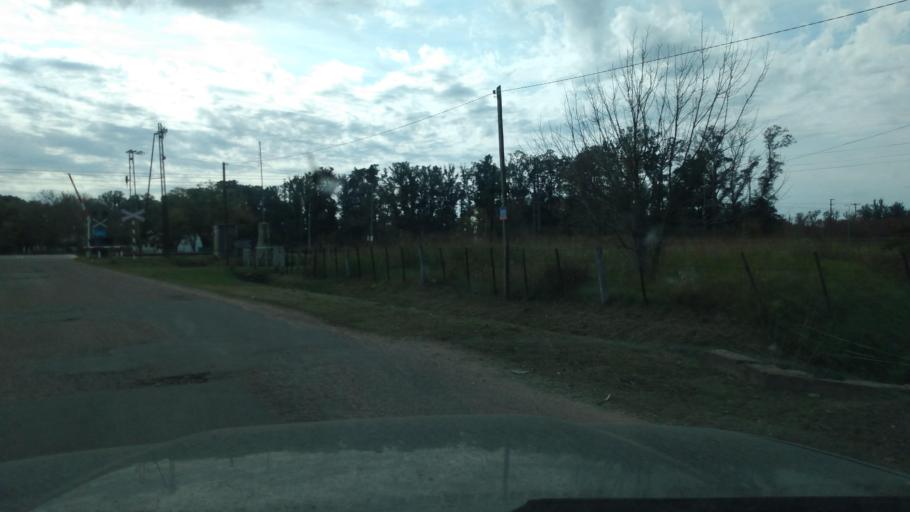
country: AR
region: Buenos Aires
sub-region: Partido de Lujan
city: Lujan
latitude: -34.6004
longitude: -59.1702
